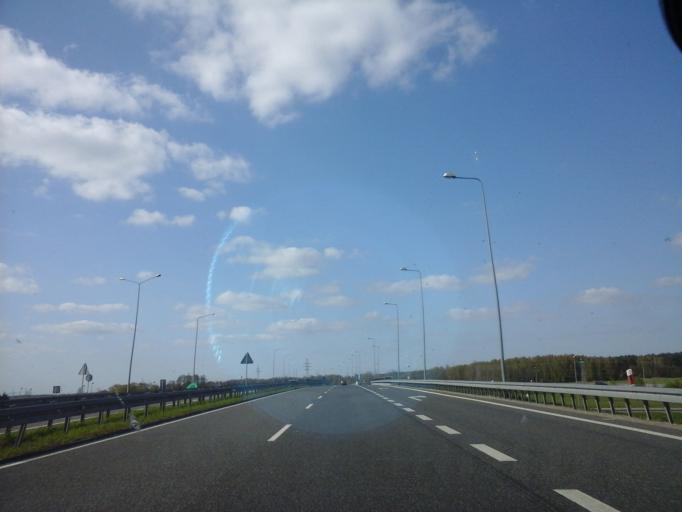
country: PL
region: West Pomeranian Voivodeship
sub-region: Powiat stargardzki
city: Kobylanka
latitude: 53.3470
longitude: 14.9506
